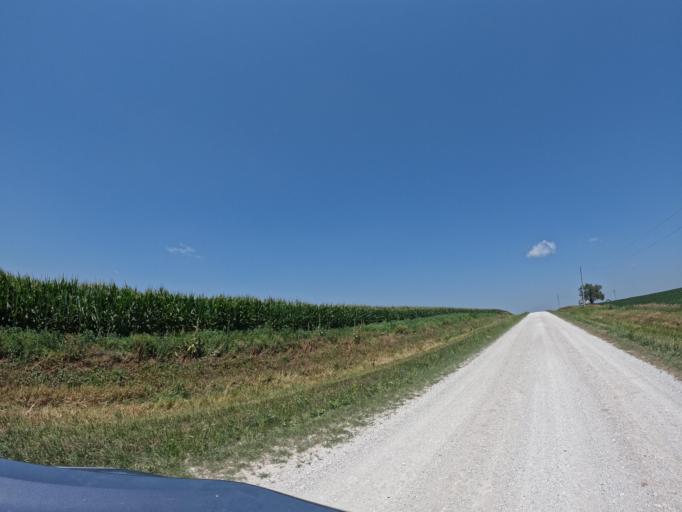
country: US
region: Iowa
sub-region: Keokuk County
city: Sigourney
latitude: 41.2629
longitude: -92.1698
